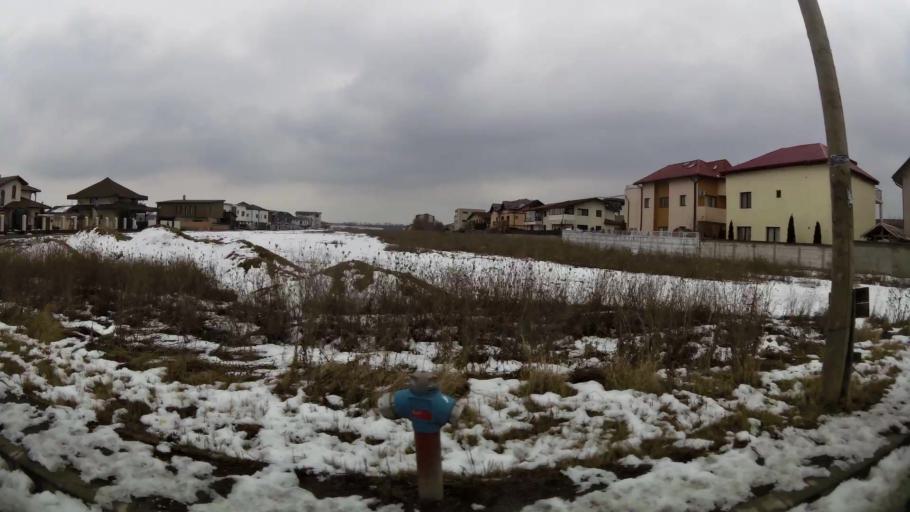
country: RO
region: Ilfov
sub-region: Comuna Otopeni
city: Otopeni
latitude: 44.5526
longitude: 26.0971
